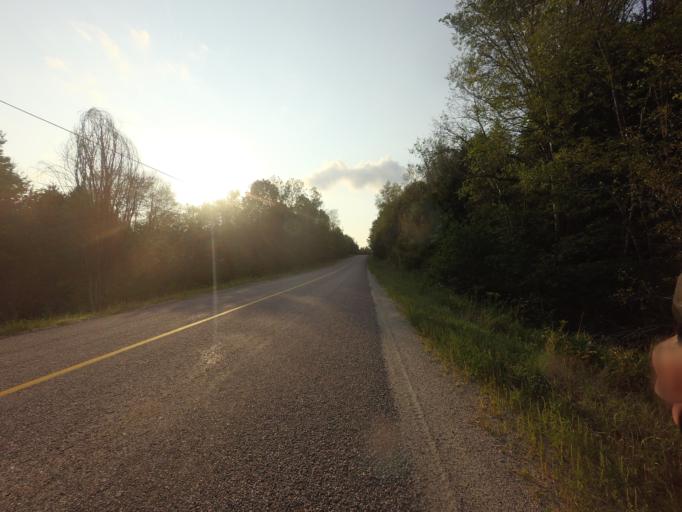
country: CA
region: Ontario
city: Renfrew
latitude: 45.0019
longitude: -76.7530
